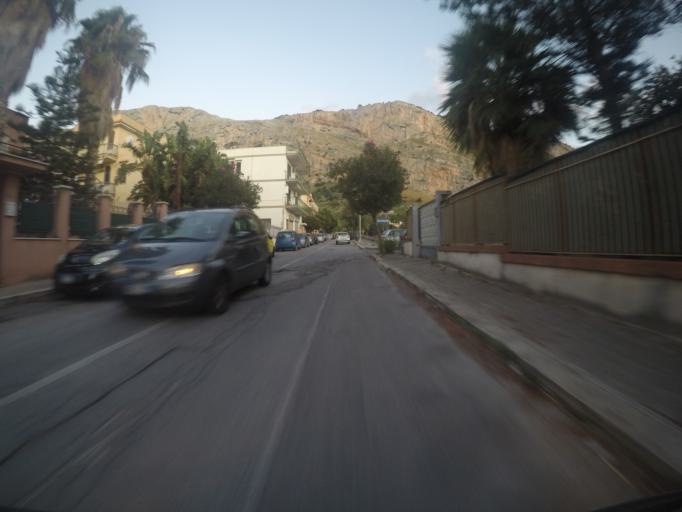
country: IT
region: Sicily
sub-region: Palermo
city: Capaci
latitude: 38.1799
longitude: 13.2432
